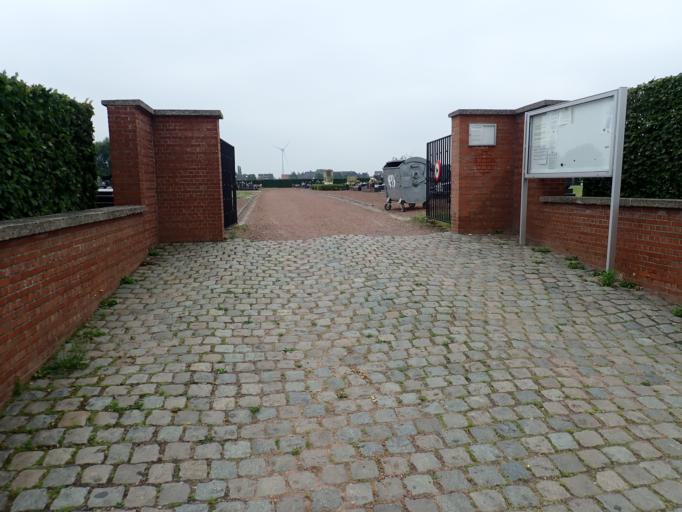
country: BE
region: Flanders
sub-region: Provincie Oost-Vlaanderen
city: Lebbeke
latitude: 51.0371
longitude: 4.1567
